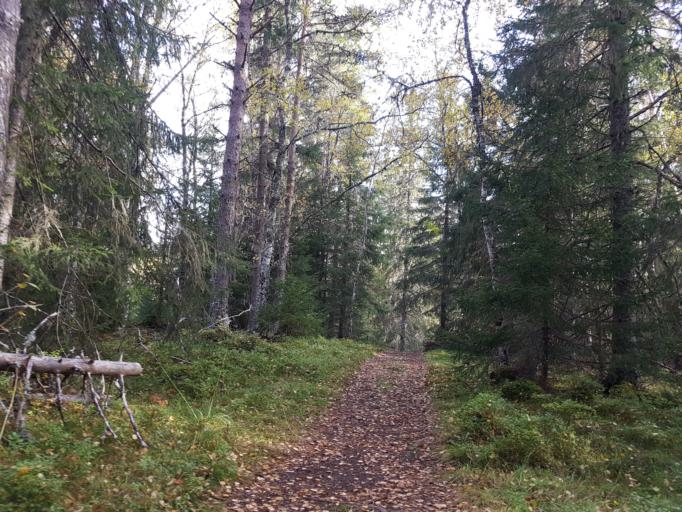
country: NO
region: Sor-Trondelag
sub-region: Trondheim
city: Trondheim
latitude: 63.4448
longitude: 10.2840
